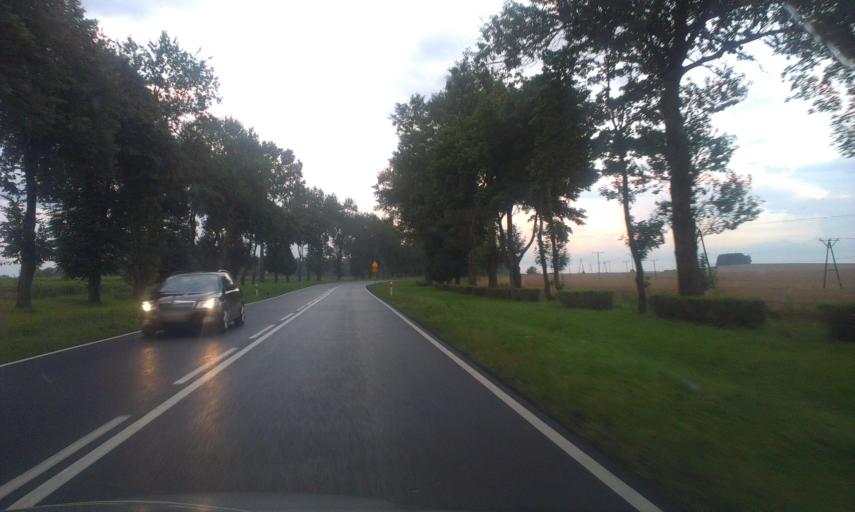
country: PL
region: West Pomeranian Voivodeship
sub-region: Koszalin
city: Koszalin
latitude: 54.1531
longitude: 16.2389
